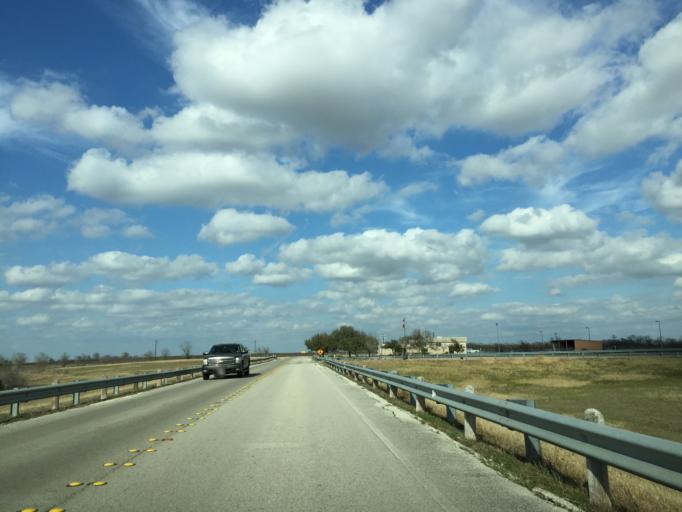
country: US
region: Texas
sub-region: Williamson County
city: Granger
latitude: 30.7167
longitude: -97.3225
